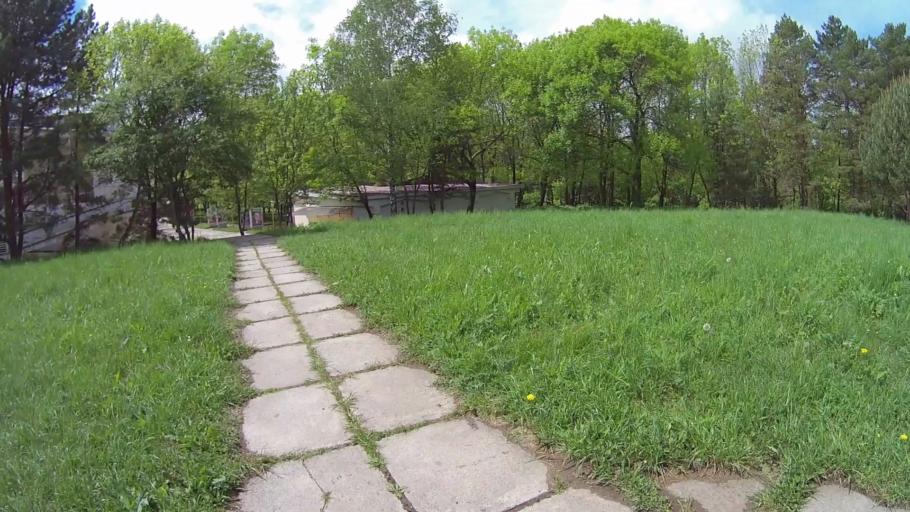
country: RU
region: Stavropol'skiy
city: Kislovodsk
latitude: 43.8983
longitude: 42.7371
